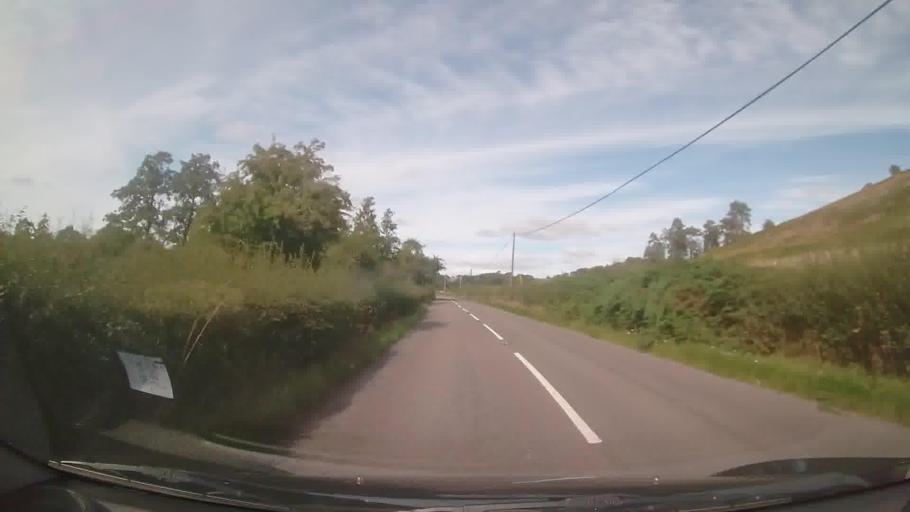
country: GB
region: England
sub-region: Shropshire
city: Lydham
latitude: 52.5633
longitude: -2.9972
